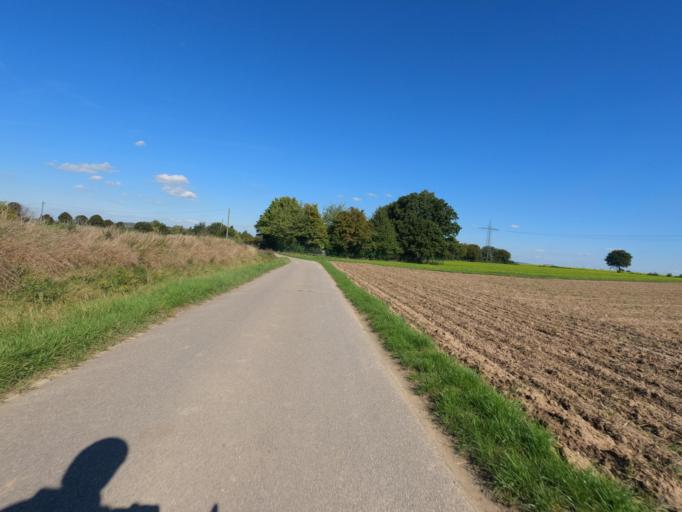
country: DE
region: North Rhine-Westphalia
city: Siersdorf
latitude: 50.8868
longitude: 6.2088
